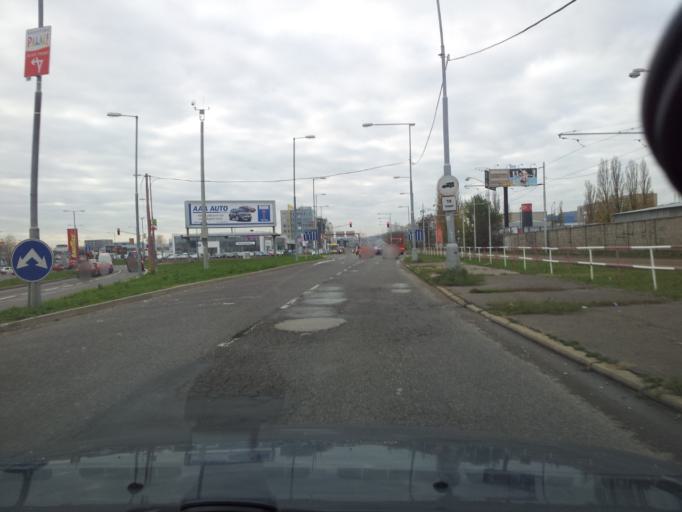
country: SK
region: Bratislavsky
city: Svaty Jur
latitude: 48.1875
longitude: 17.1760
